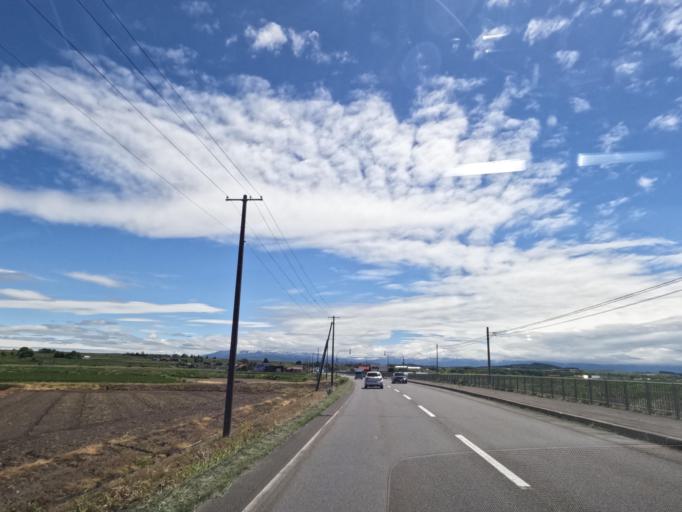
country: JP
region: Hokkaido
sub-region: Asahikawa-shi
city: Asahikawa
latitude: 43.6654
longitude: 142.4144
